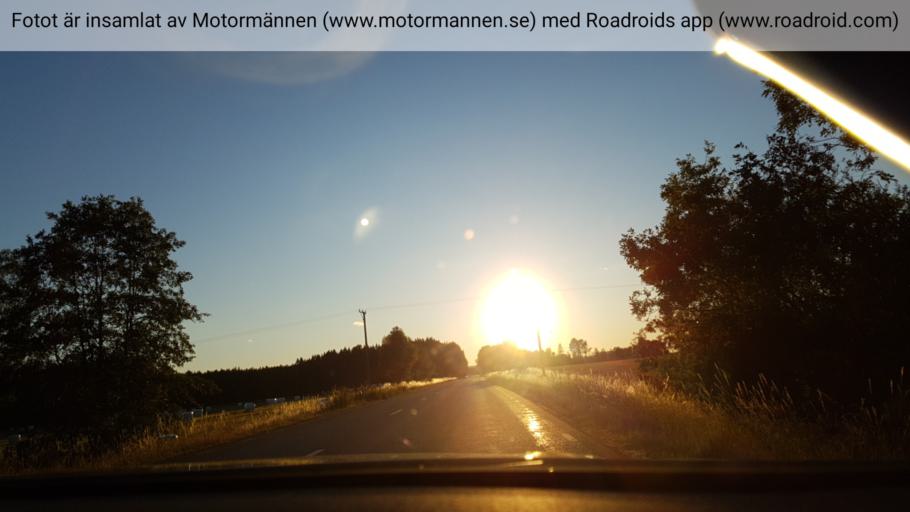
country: SE
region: Vaestra Goetaland
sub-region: Tidaholms Kommun
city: Olofstorp
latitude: 58.3660
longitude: 14.0186
